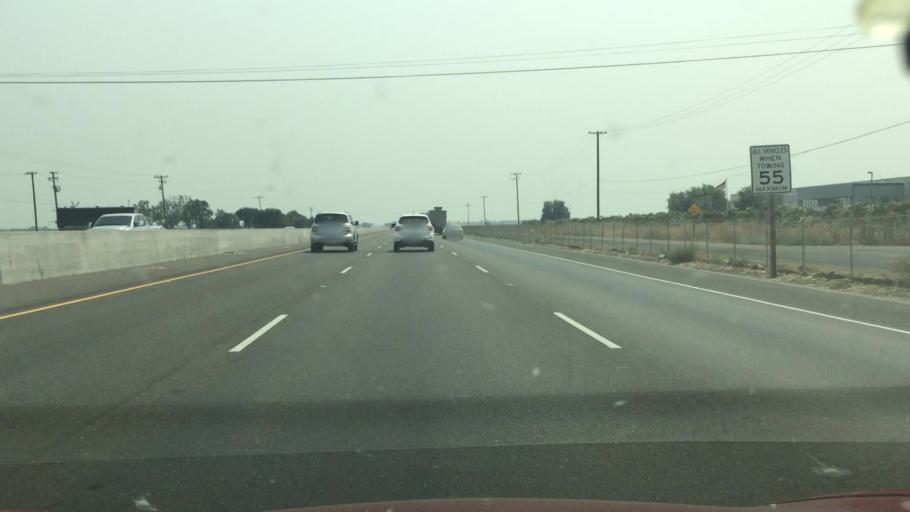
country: US
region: California
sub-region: San Joaquin County
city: Kennedy
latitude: 37.8920
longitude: -121.2205
